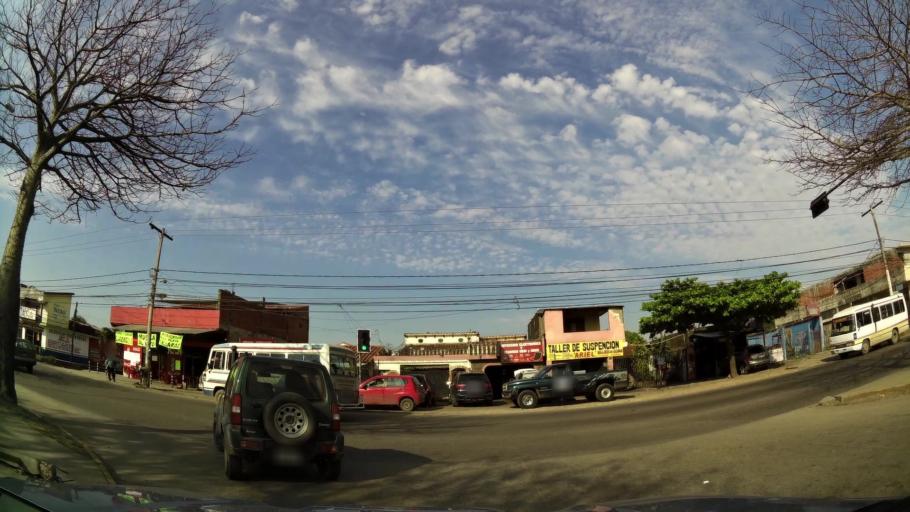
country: BO
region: Santa Cruz
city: Santa Cruz de la Sierra
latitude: -17.7543
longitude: -63.1583
